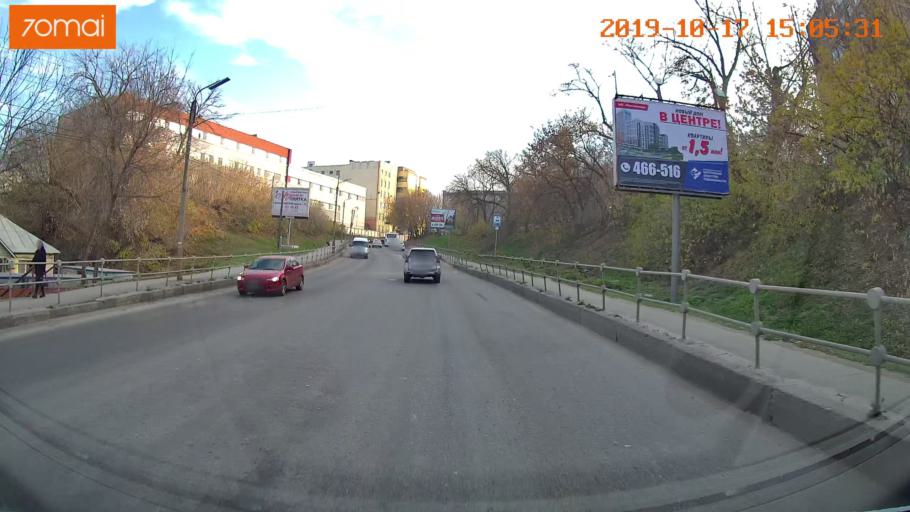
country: RU
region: Rjazan
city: Ryazan'
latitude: 54.6351
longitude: 39.7235
